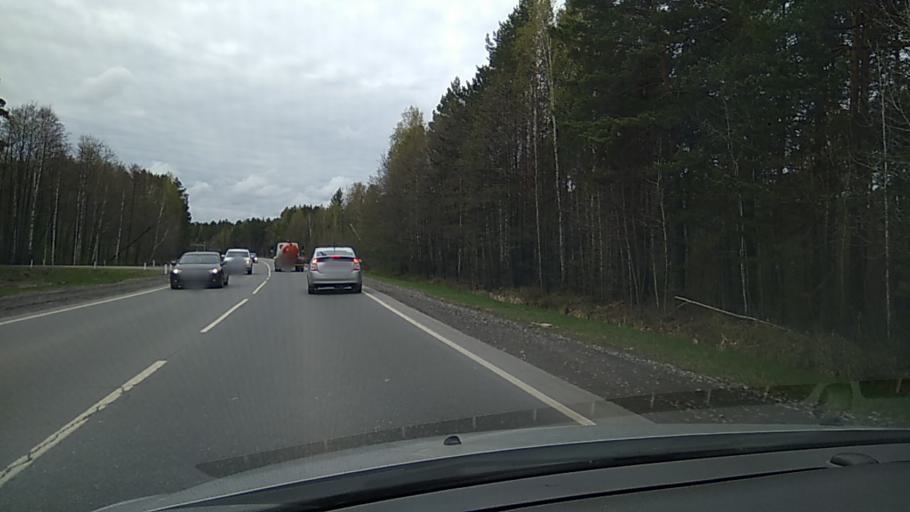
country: RU
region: Tjumen
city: Chervishevo
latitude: 56.9722
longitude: 65.4403
